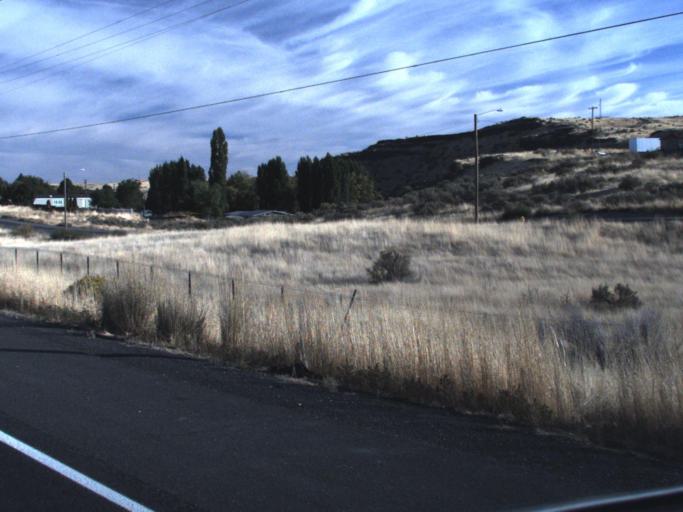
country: US
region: Washington
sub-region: Franklin County
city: Basin City
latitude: 46.5750
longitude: -119.0040
